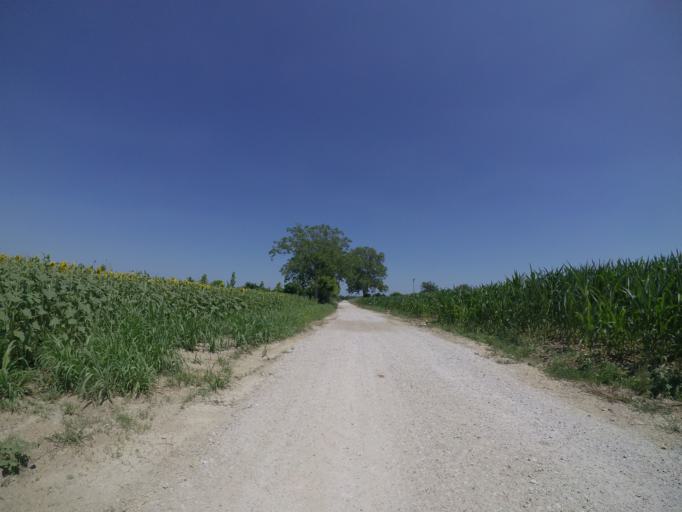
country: IT
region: Friuli Venezia Giulia
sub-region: Provincia di Udine
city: Talmassons
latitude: 45.9278
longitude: 13.0958
